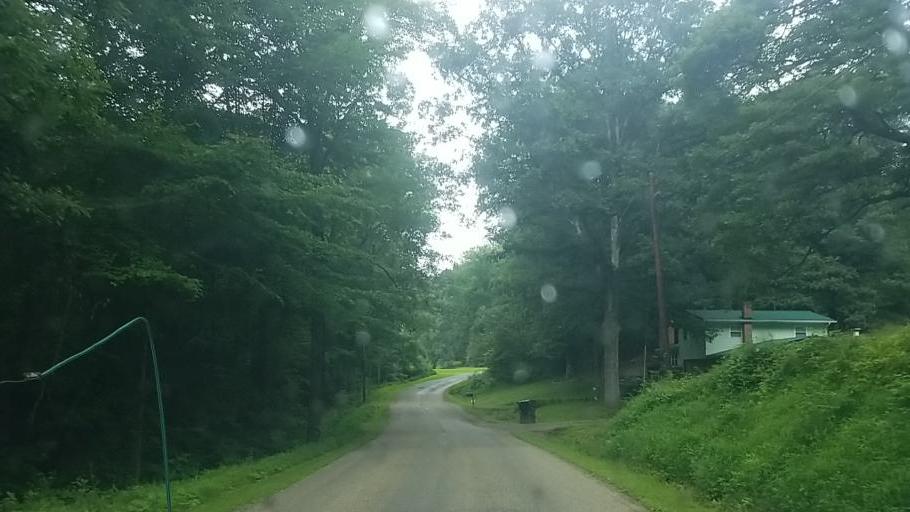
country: US
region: Ohio
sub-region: Muskingum County
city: Frazeysburg
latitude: 40.1542
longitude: -82.2640
